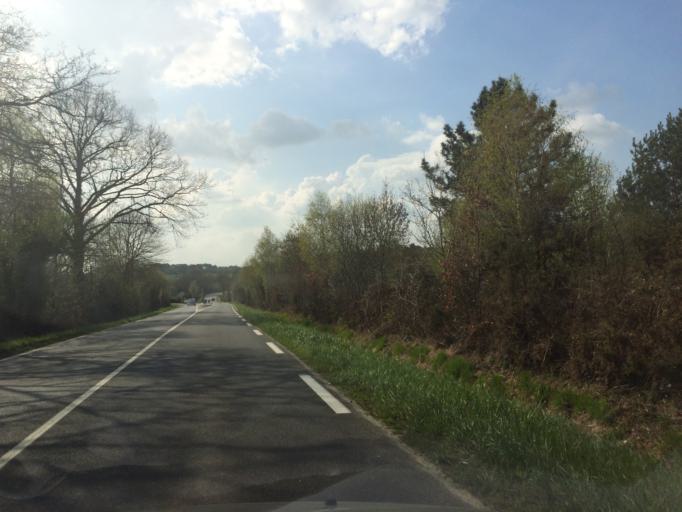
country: FR
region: Pays de la Loire
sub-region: Departement de la Loire-Atlantique
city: Bouvron
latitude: 47.4855
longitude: -1.8452
